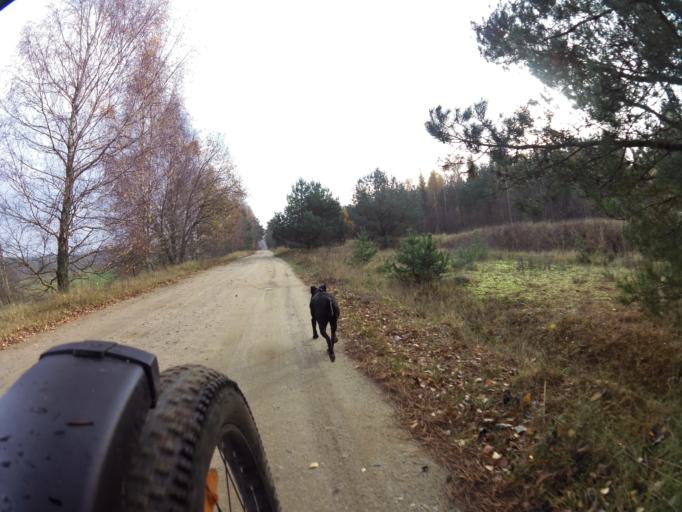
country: PL
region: Pomeranian Voivodeship
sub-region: Powiat wejherowski
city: Orle
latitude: 54.7032
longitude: 18.1067
